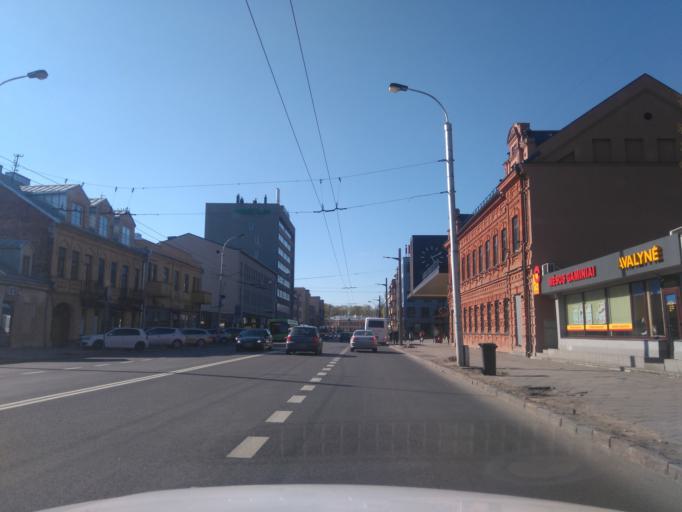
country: LT
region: Kauno apskritis
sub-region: Kaunas
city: Aleksotas
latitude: 54.8885
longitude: 23.9283
